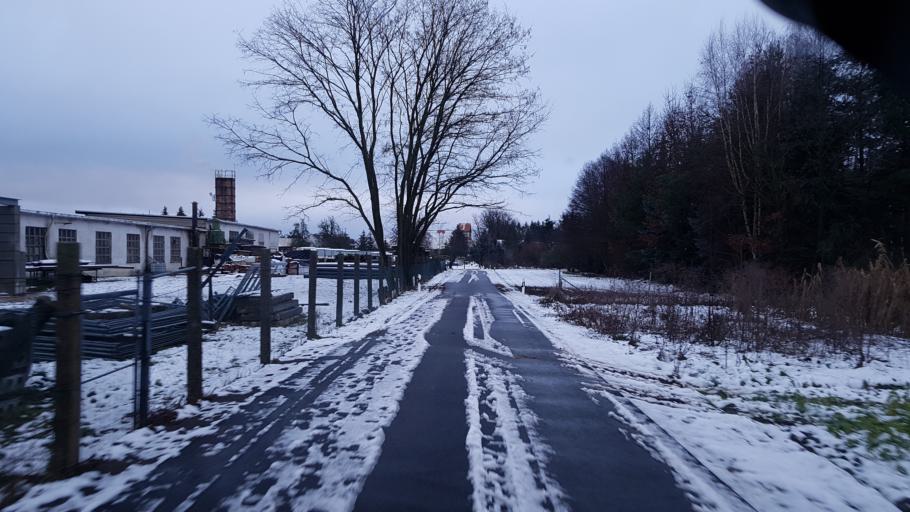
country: DE
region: Brandenburg
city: Luckau
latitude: 51.7752
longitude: 13.6929
